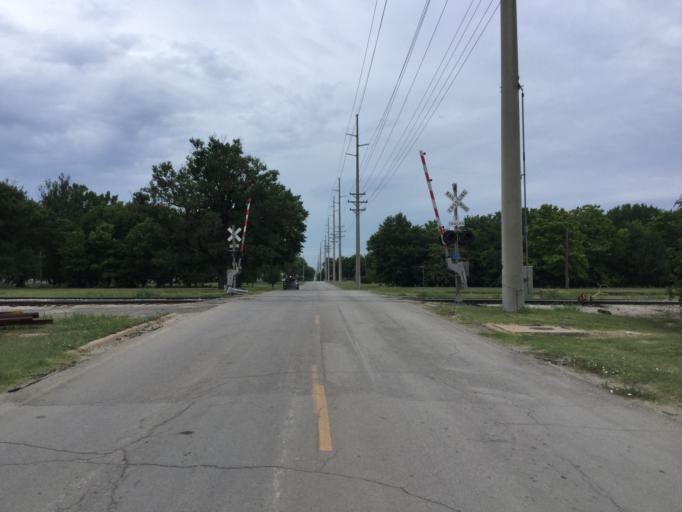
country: US
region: Kansas
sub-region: Montgomery County
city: Coffeyville
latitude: 37.0434
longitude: -95.6113
